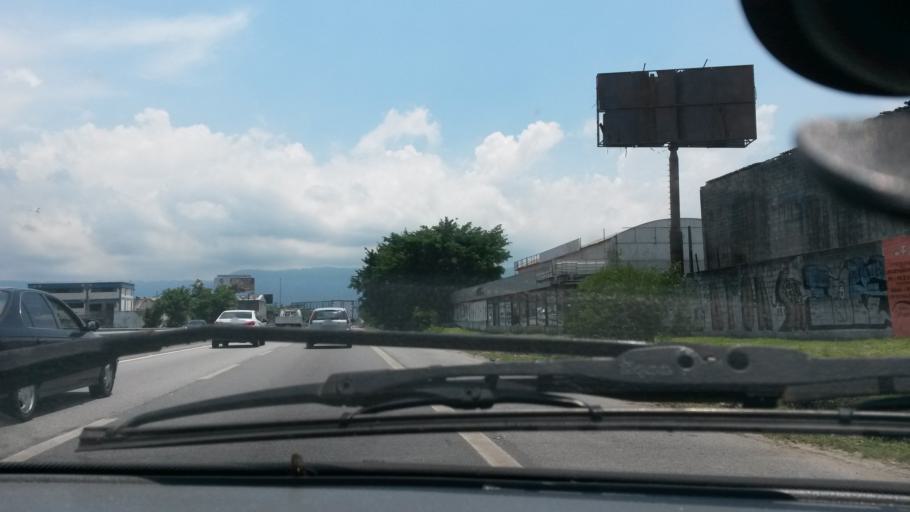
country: BR
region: Sao Paulo
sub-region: Sao Vicente
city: Sao Vicente
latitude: -23.9493
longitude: -46.4139
